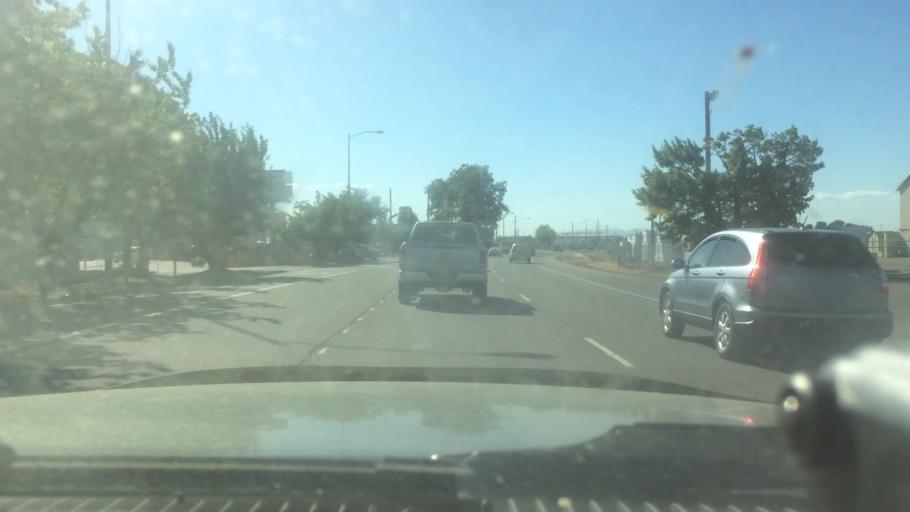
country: US
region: Oregon
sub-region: Lane County
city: Eugene
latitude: 44.0545
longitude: -123.1254
